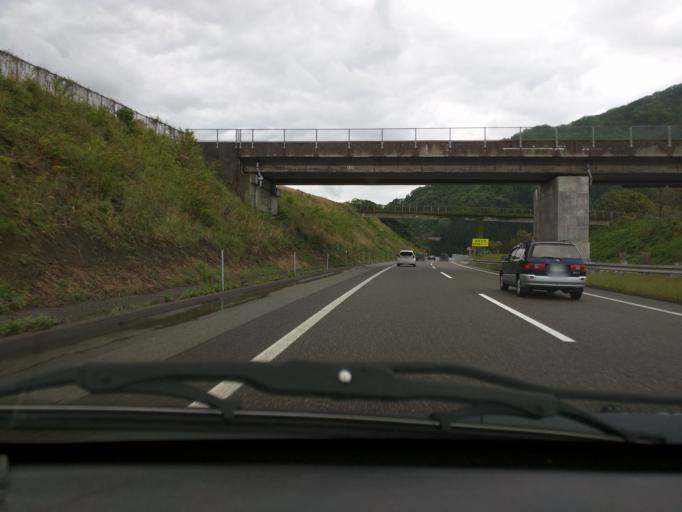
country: JP
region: Niigata
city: Kashiwazaki
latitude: 37.3253
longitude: 138.4596
